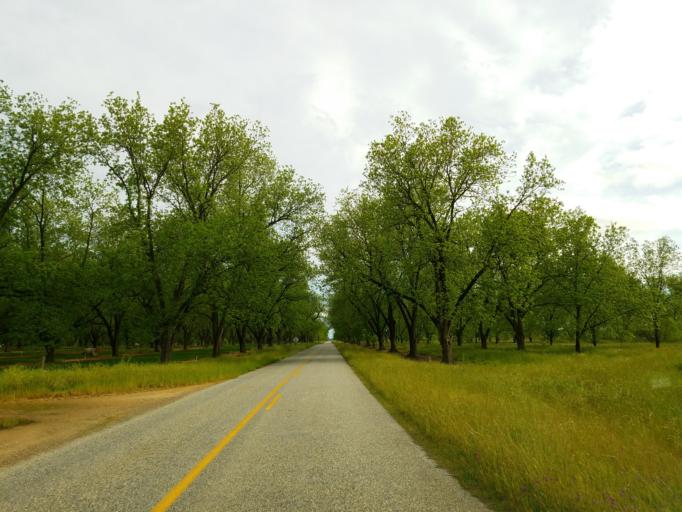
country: US
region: Georgia
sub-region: Dooly County
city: Vienna
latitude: 32.1602
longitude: -83.7607
